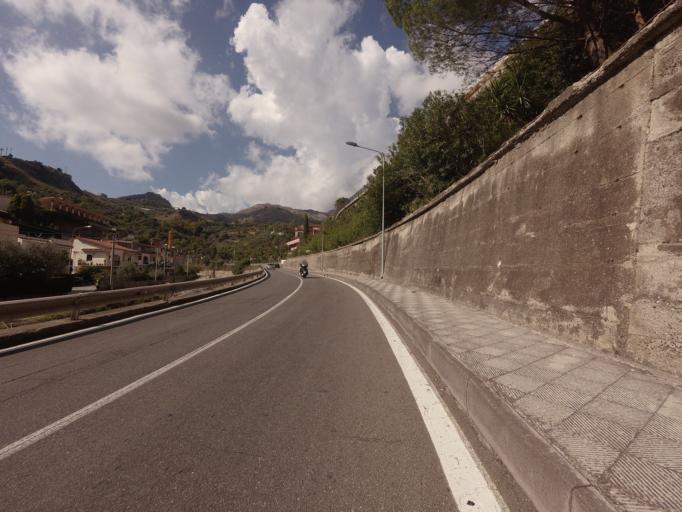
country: IT
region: Sicily
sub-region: Messina
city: Taormina
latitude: 37.8452
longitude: 15.2789
